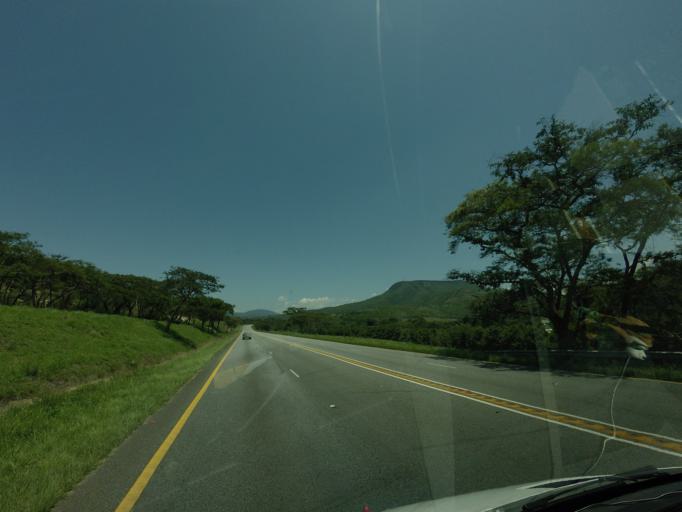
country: ZA
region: Mpumalanga
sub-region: Ehlanzeni District
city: Nelspruit
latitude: -25.4274
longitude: 30.7819
